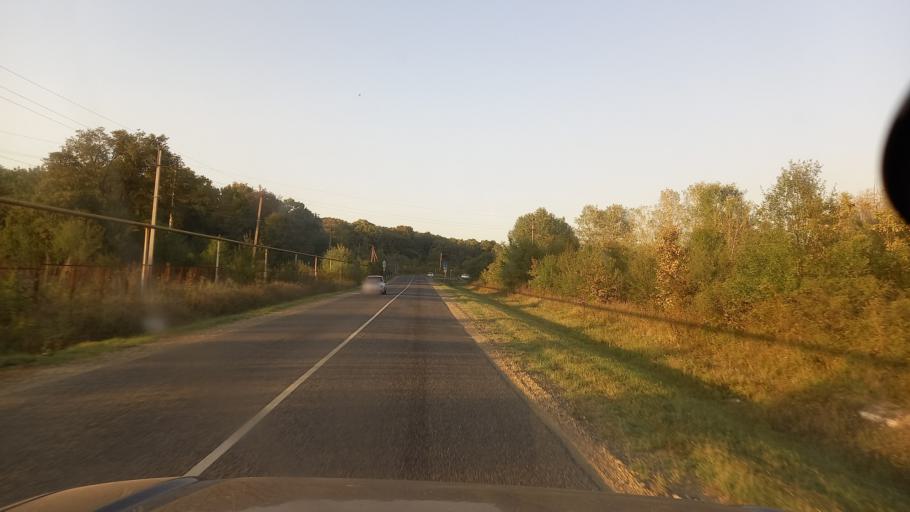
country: RU
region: Krasnodarskiy
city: Smolenskaya
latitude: 44.7598
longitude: 38.7686
